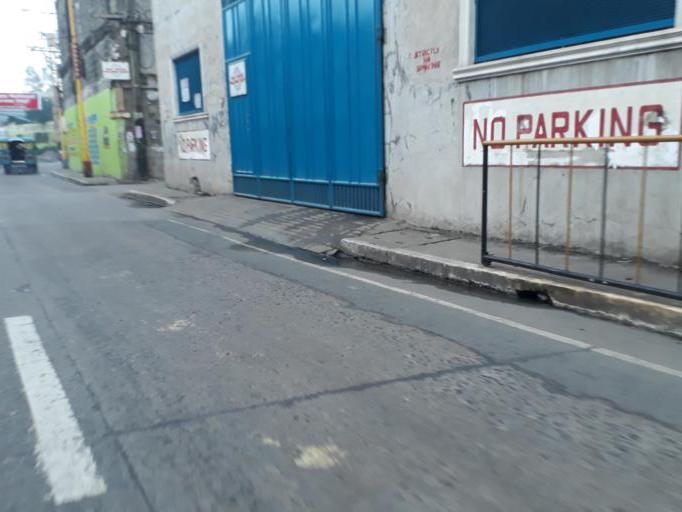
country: PH
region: Calabarzon
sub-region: Province of Rizal
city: Malabon
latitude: 14.6704
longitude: 120.9409
